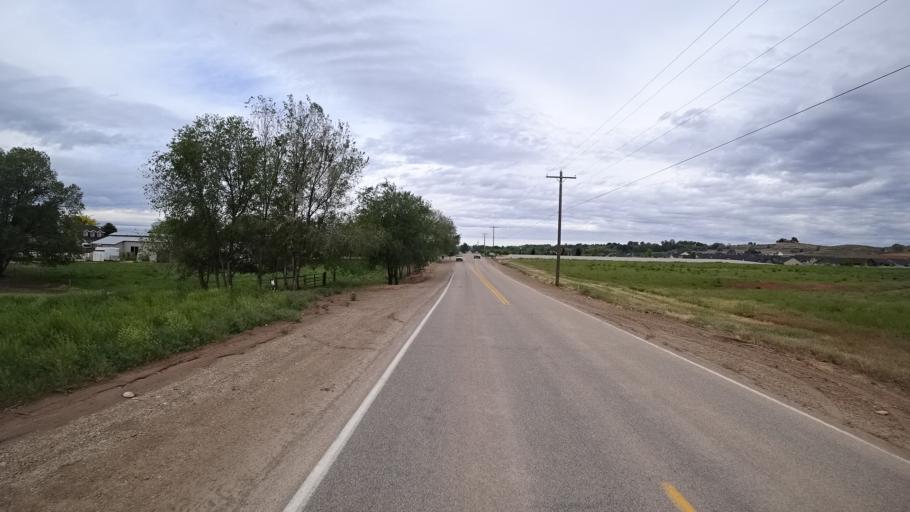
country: US
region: Idaho
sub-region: Ada County
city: Star
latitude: 43.7175
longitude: -116.4916
